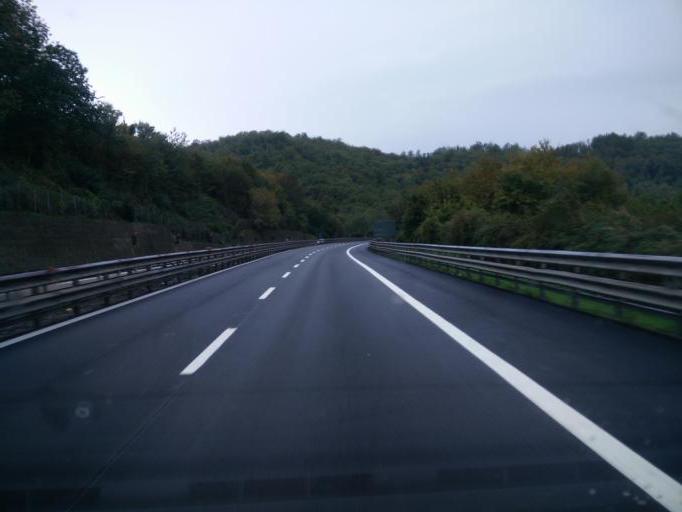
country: IT
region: Tuscany
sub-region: Province of Florence
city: Barberino di Mugello
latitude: 44.0544
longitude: 11.2143
